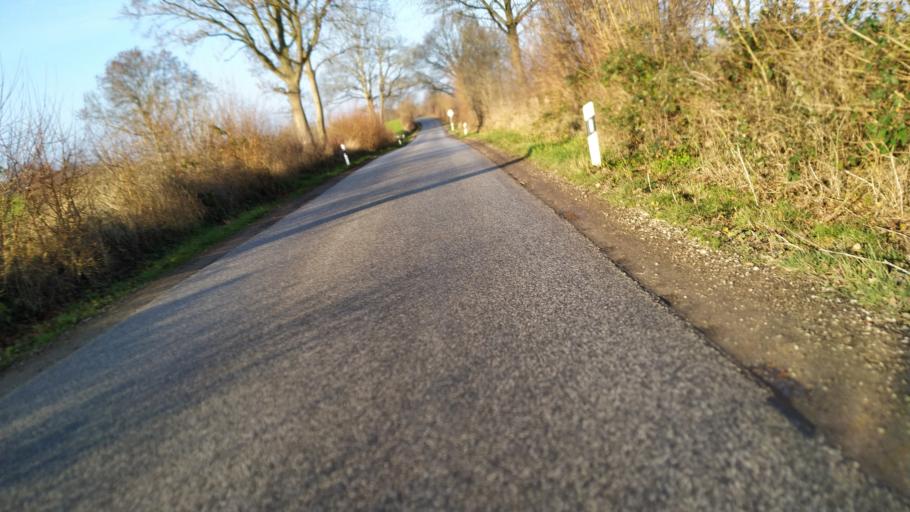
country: DE
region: Schleswig-Holstein
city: Travemuende
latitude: 53.9650
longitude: 10.8320
